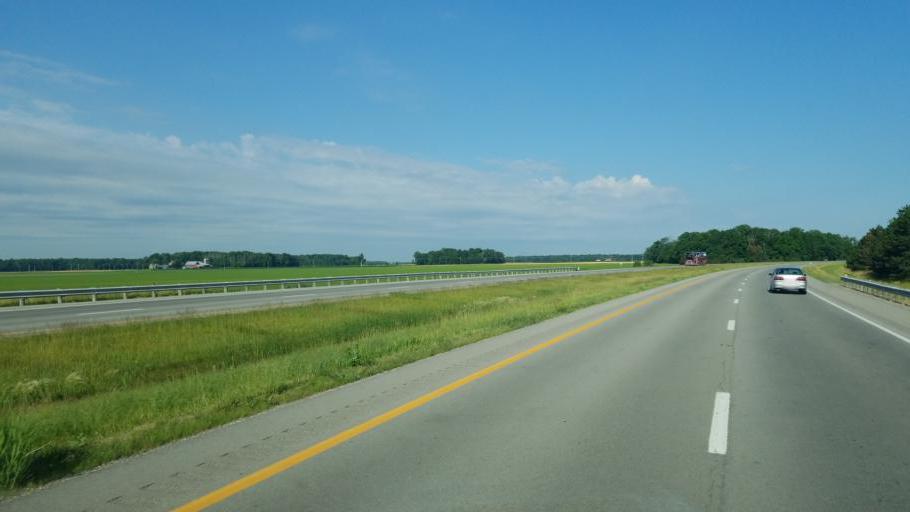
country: US
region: Ohio
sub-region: Hancock County
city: Findlay
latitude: 40.9820
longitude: -83.5450
